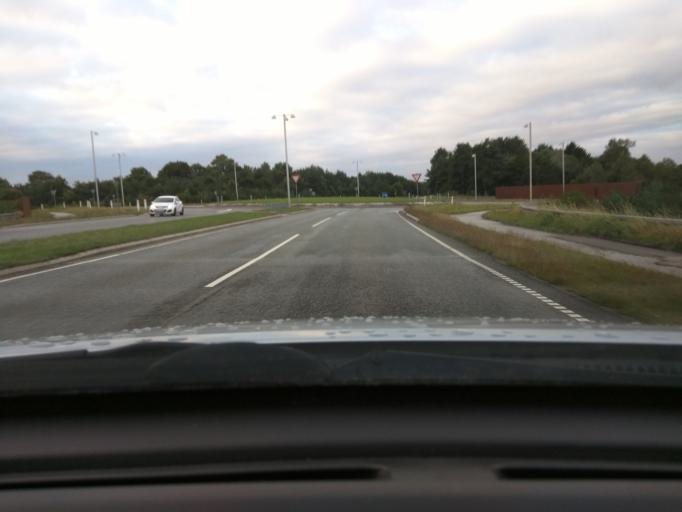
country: DK
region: Central Jutland
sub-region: Viborg Kommune
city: Viborg
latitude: 56.4275
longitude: 9.3899
